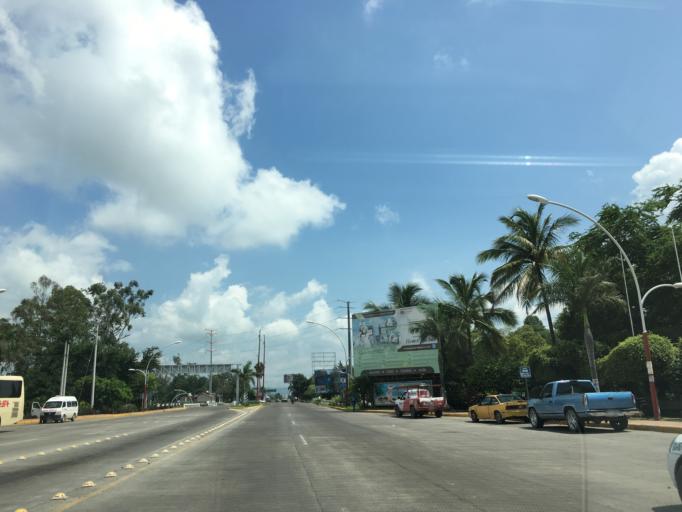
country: MX
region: Nayarit
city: Xalisco
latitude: 21.4723
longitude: -104.8894
